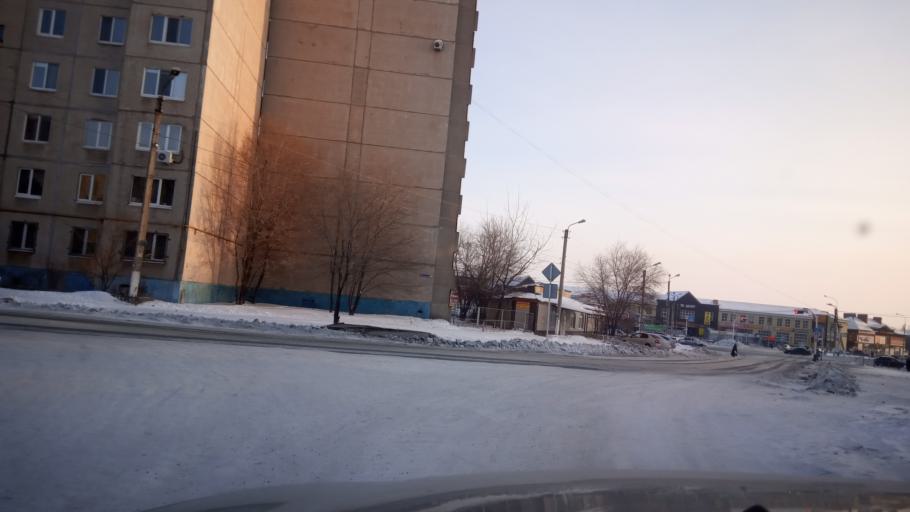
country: RU
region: Orenburg
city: Novotroitsk
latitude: 51.1931
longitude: 58.2907
